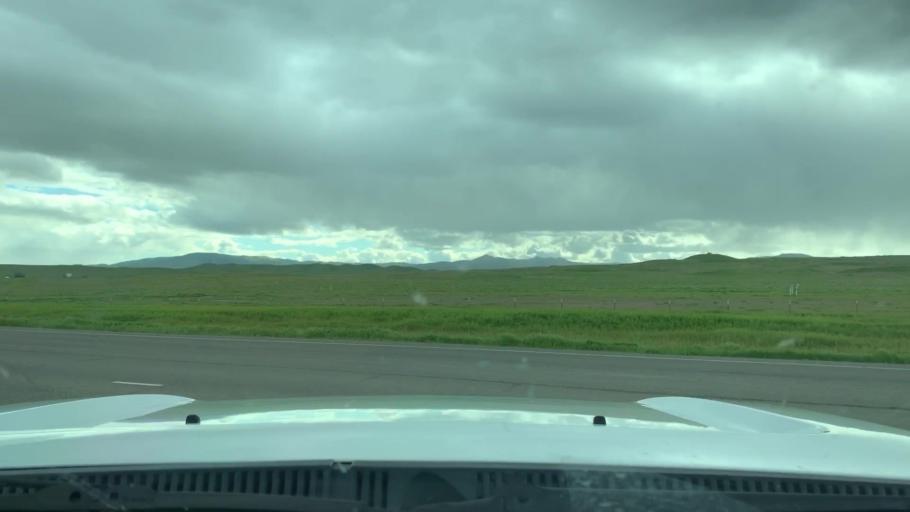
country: US
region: California
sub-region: Kings County
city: Avenal
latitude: 35.8910
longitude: -120.0474
